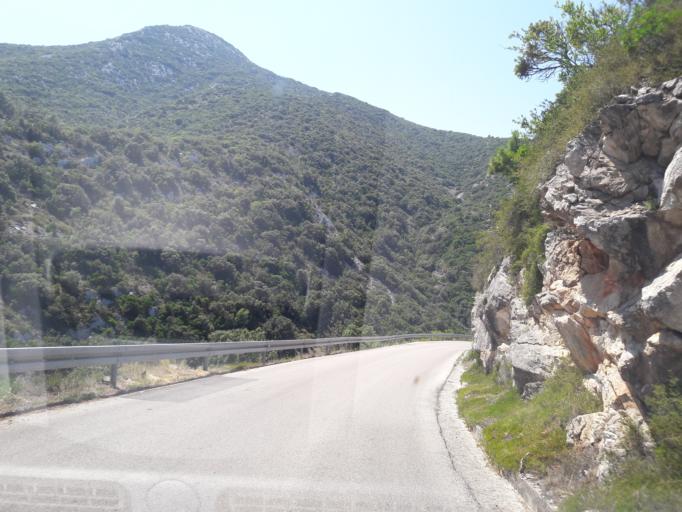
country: HR
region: Dubrovacko-Neretvanska
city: Orebic
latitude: 43.0109
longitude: 17.2022
